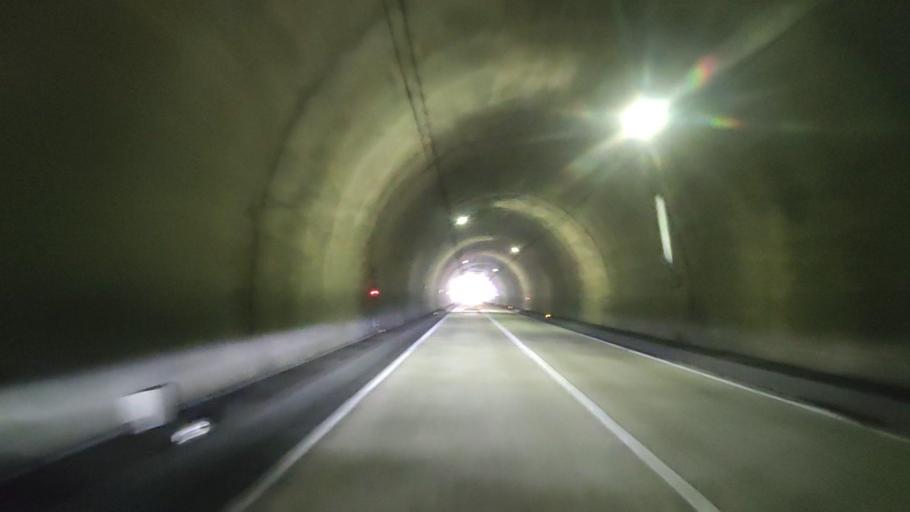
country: JP
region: Nara
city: Yoshino-cho
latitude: 34.2111
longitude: 135.9984
